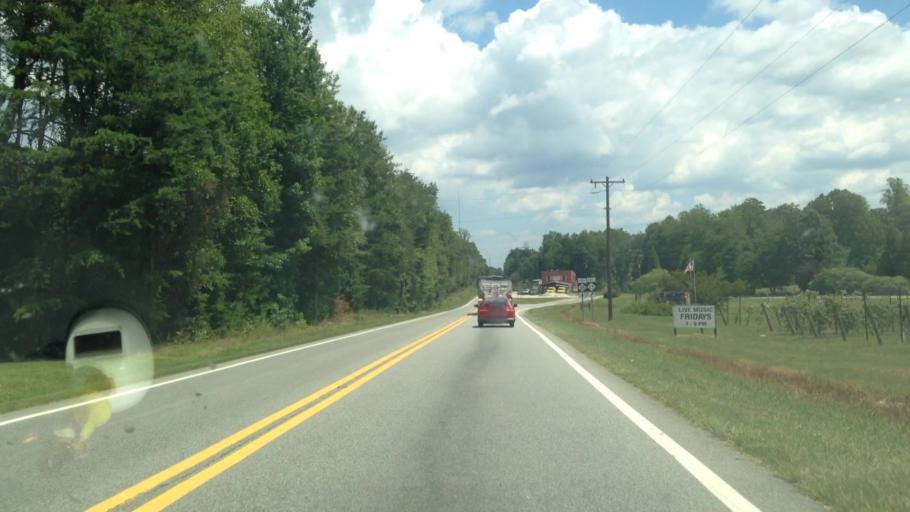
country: US
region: North Carolina
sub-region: Guilford County
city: Stokesdale
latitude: 36.2522
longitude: -79.9655
